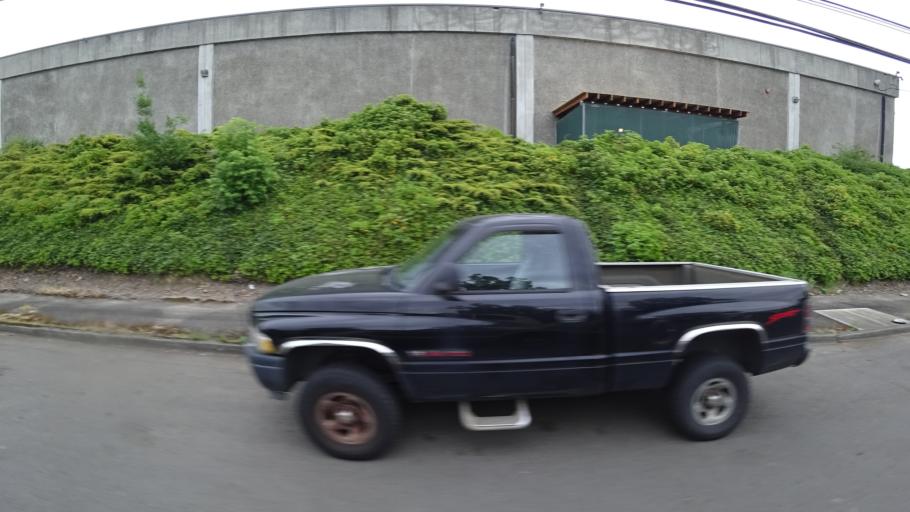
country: US
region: Oregon
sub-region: Washington County
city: Beaverton
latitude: 45.4780
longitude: -122.7874
